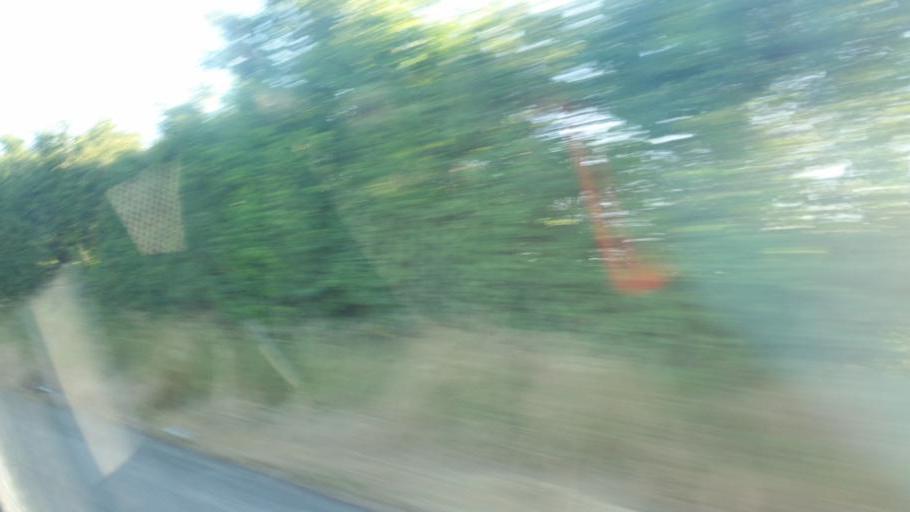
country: IE
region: Leinster
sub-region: Fingal County
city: Blanchardstown
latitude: 53.4486
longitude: -6.3437
